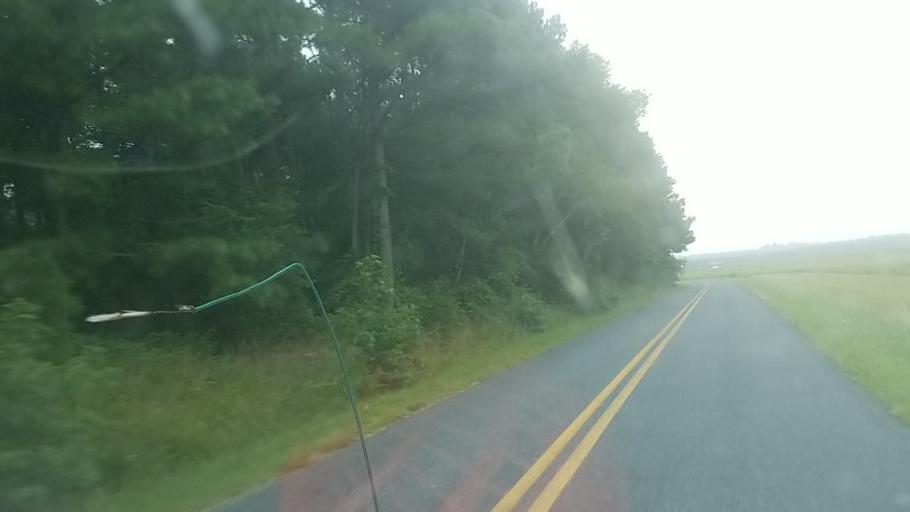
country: US
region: Maryland
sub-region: Wicomico County
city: Delmar
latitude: 38.4142
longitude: -75.5013
